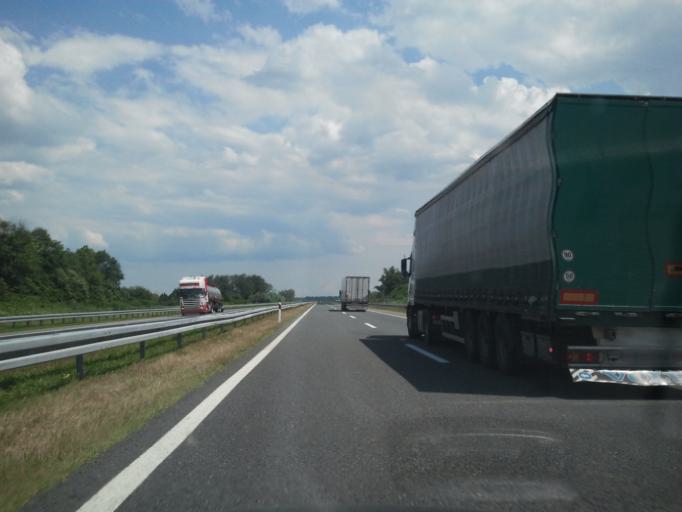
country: HR
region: Brodsko-Posavska
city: Sikirevci
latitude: 45.1160
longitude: 18.4905
